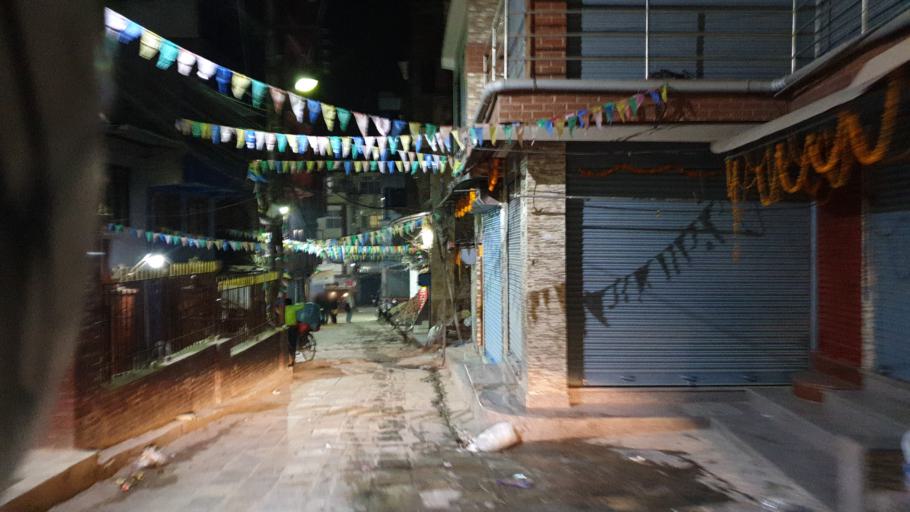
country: NP
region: Central Region
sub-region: Bagmati Zone
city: Kathmandu
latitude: 27.6979
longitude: 85.3084
